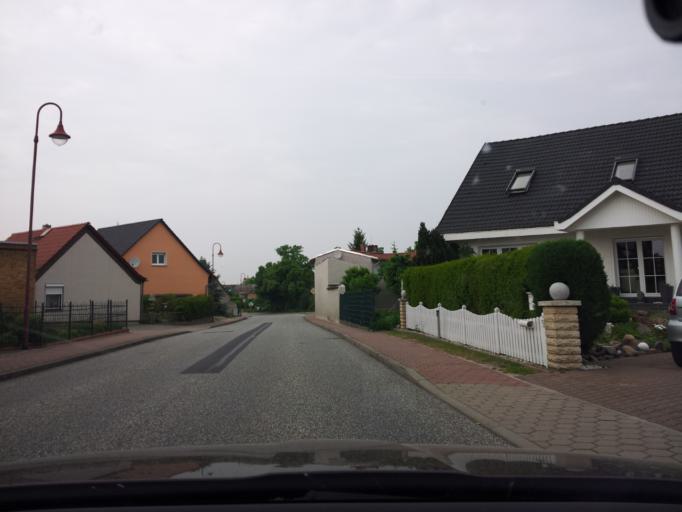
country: DE
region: Brandenburg
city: Linthe
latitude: 52.1534
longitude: 12.7869
